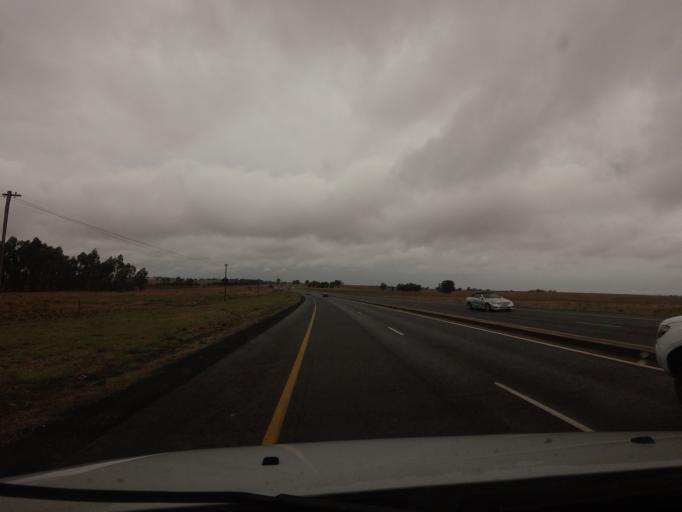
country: ZA
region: Mpumalanga
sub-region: Nkangala District Municipality
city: Belfast
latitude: -25.7641
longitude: 29.9722
